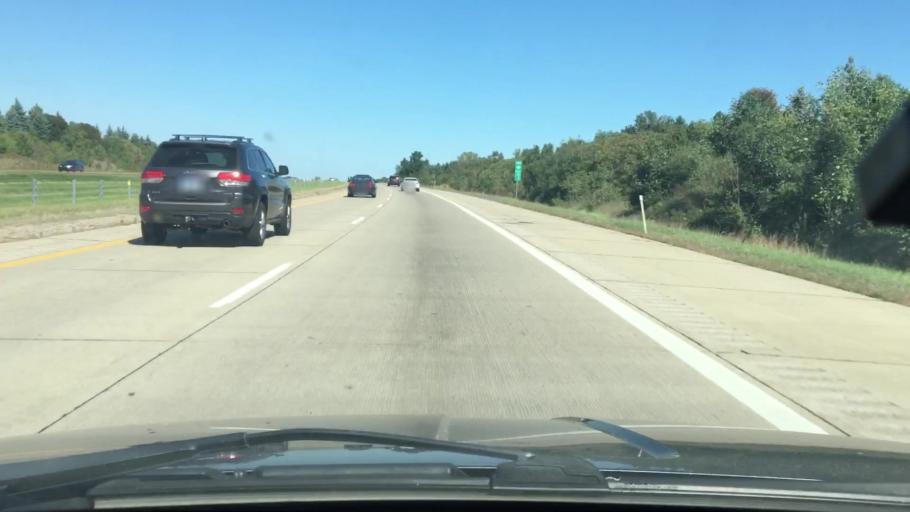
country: US
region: Michigan
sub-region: Wayne County
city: Plymouth
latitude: 42.3703
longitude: -83.5421
